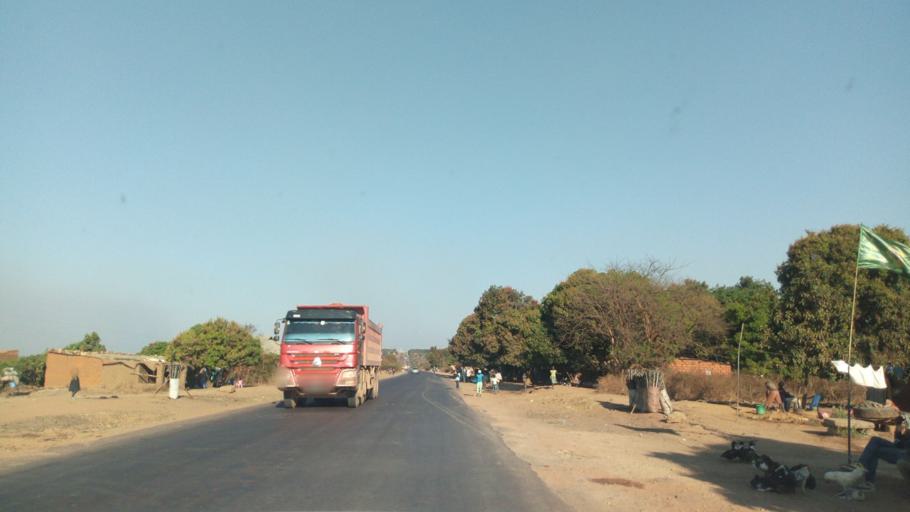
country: CD
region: Katanga
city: Likasi
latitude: -11.0482
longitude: 26.9545
